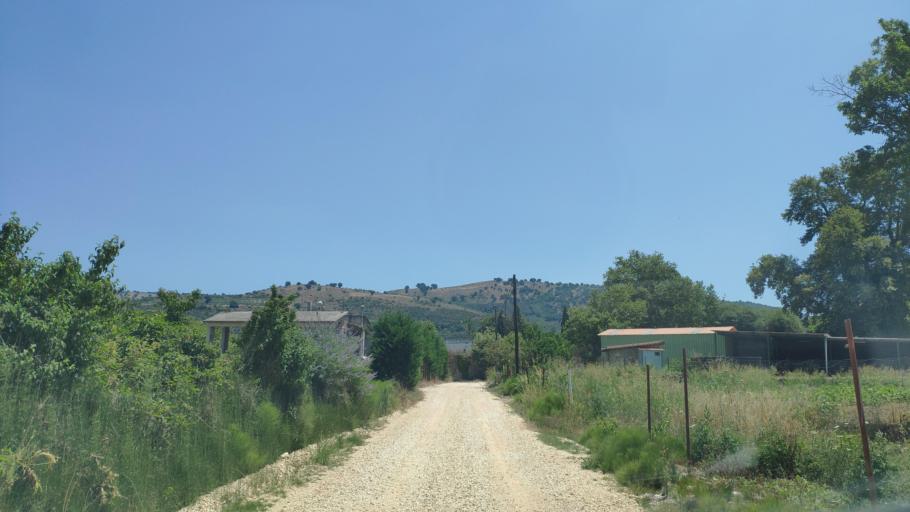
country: GR
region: West Greece
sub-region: Nomos Aitolias kai Akarnanias
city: Amfilochia
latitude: 38.8701
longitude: 21.0704
